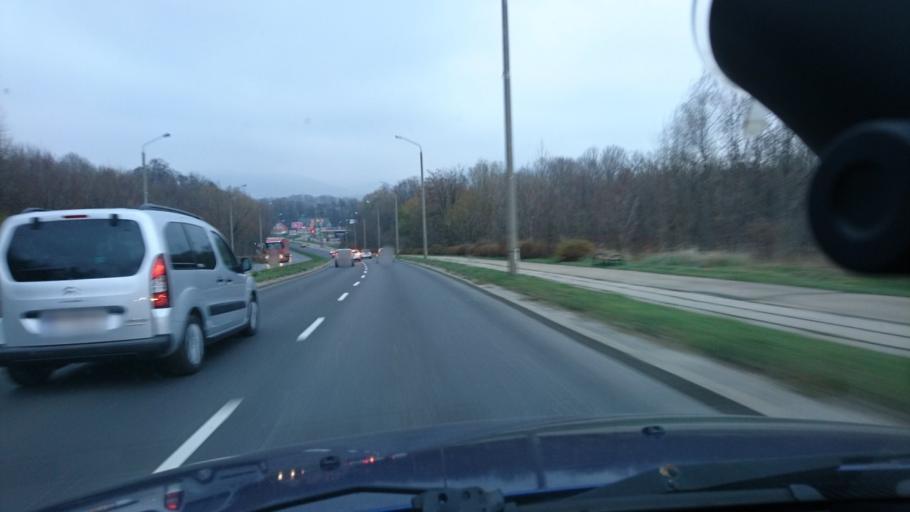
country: PL
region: Silesian Voivodeship
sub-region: Bielsko-Biala
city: Bielsko-Biala
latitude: 49.8006
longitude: 19.0345
